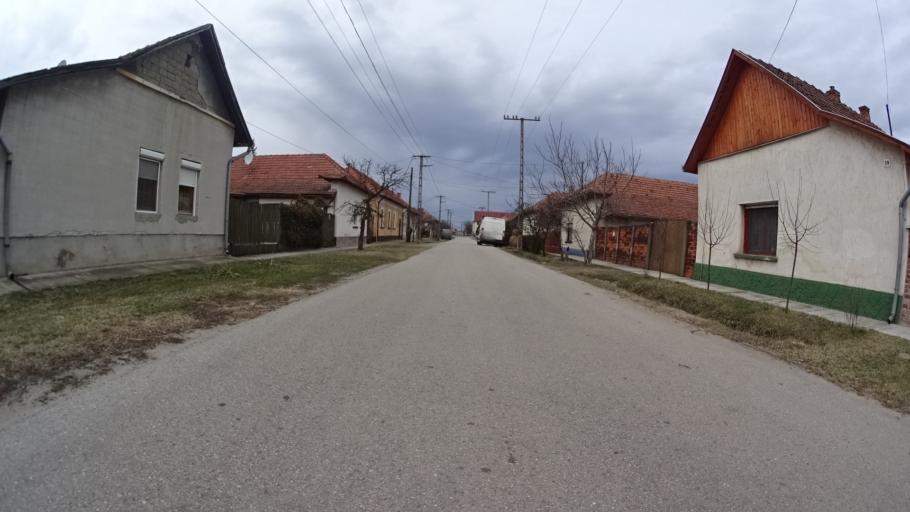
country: HU
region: Bacs-Kiskun
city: Tiszakecske
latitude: 46.9322
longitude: 20.0803
